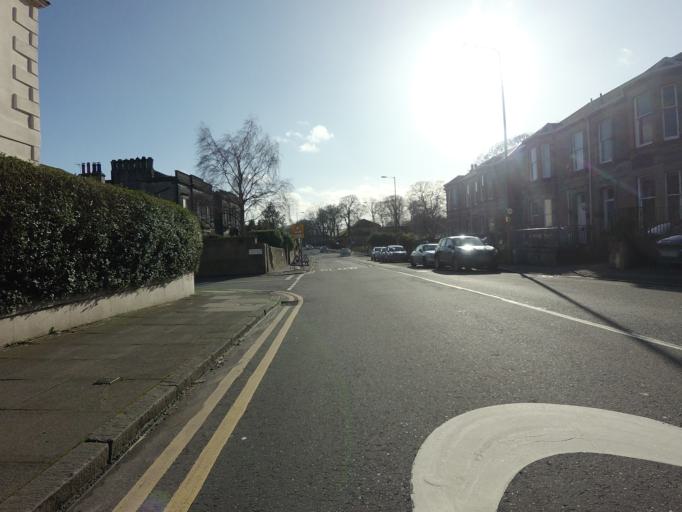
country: GB
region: Scotland
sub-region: Edinburgh
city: Edinburgh
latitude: 55.9774
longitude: -3.1928
